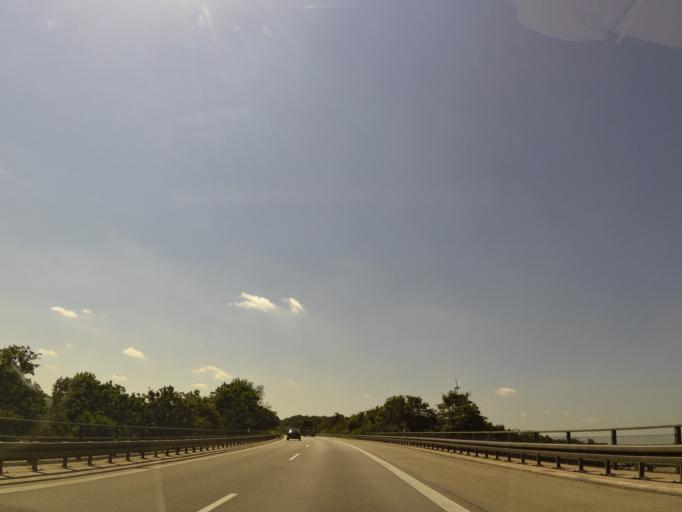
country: DE
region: Bavaria
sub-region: Upper Bavaria
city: Garching bei Munchen
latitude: 48.2241
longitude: 11.6308
